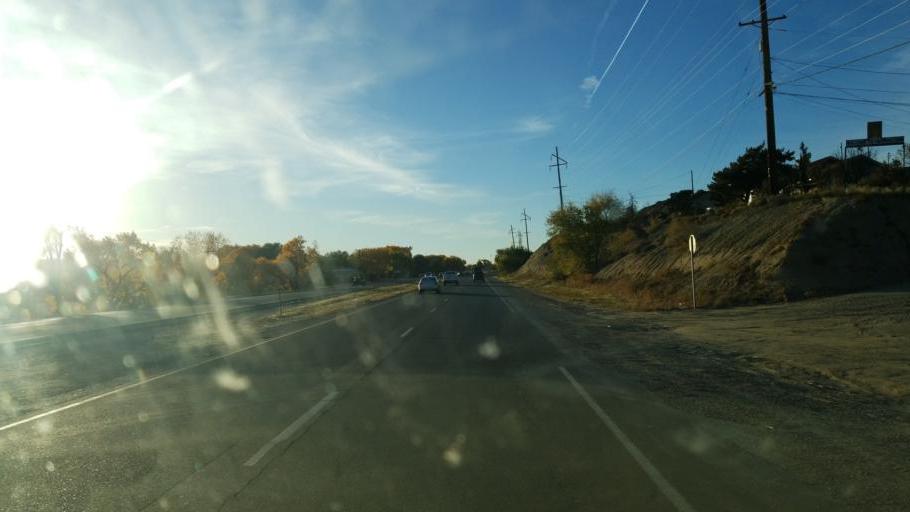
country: US
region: New Mexico
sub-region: San Juan County
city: Lee Acres
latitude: 36.7070
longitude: -108.1226
